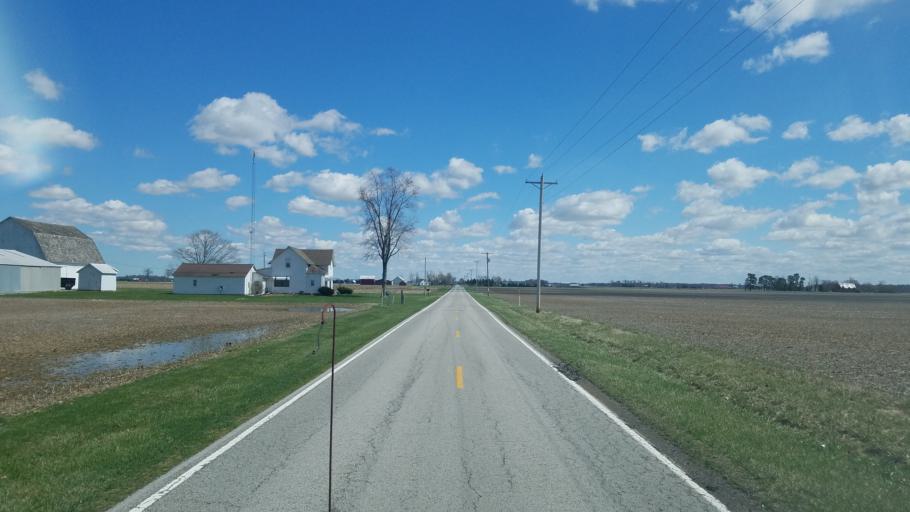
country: US
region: Ohio
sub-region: Hancock County
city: Findlay
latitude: 41.0070
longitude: -83.5447
